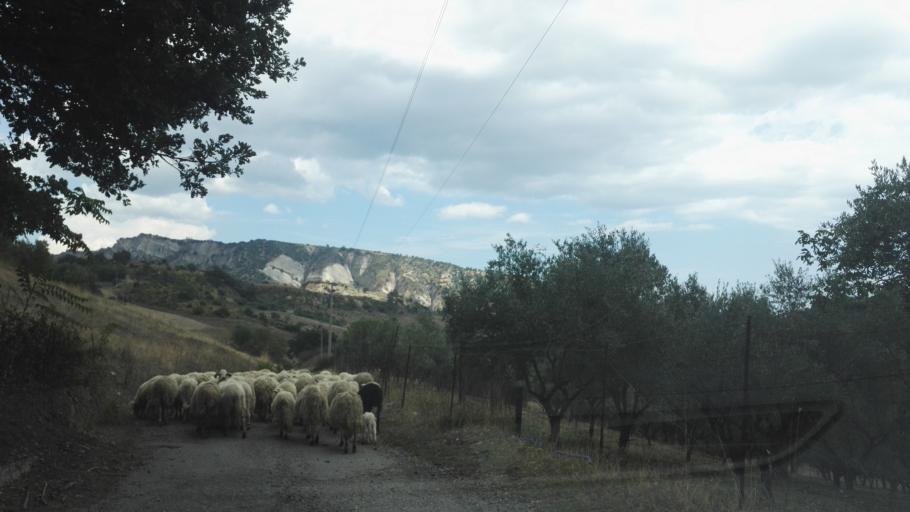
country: IT
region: Calabria
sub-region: Provincia di Reggio Calabria
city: Stilo
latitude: 38.4661
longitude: 16.4705
